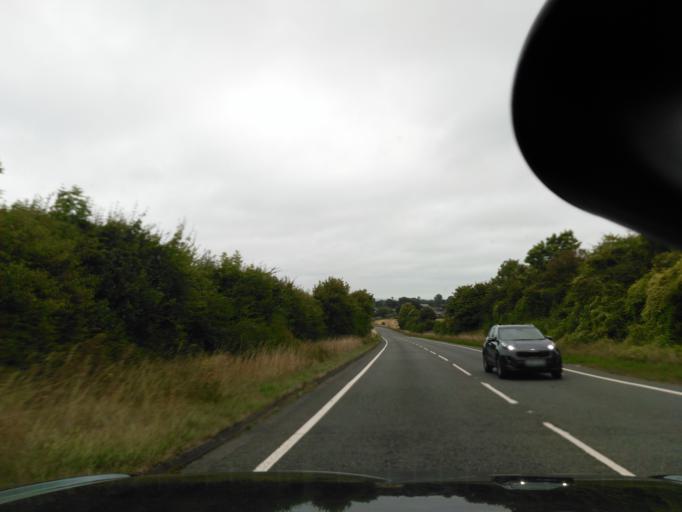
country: GB
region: England
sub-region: Wiltshire
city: Upton Scudamore
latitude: 51.2387
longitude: -2.1880
